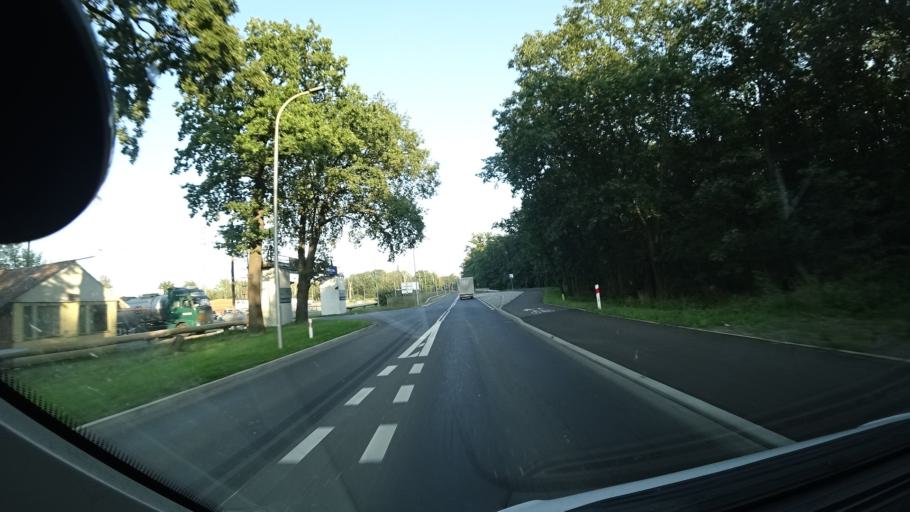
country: PL
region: Opole Voivodeship
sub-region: Powiat kedzierzynsko-kozielski
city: Bierawa
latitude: 50.2871
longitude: 18.2784
